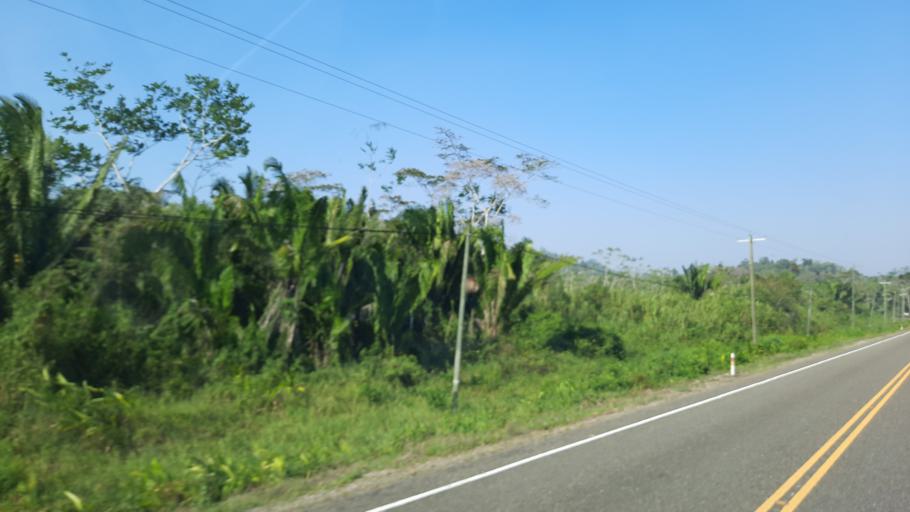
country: BZ
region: Cayo
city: Belmopan
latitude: 17.1486
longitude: -88.7222
